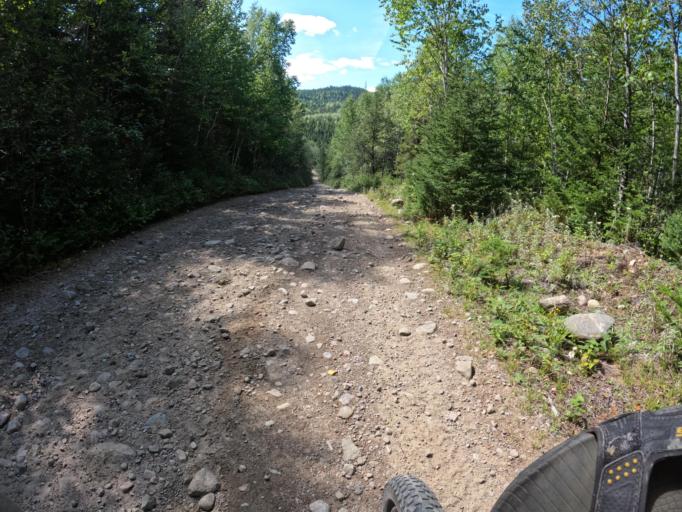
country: CA
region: Quebec
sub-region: Capitale-Nationale
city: Baie-Saint-Paul
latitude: 47.9971
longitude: -70.6601
